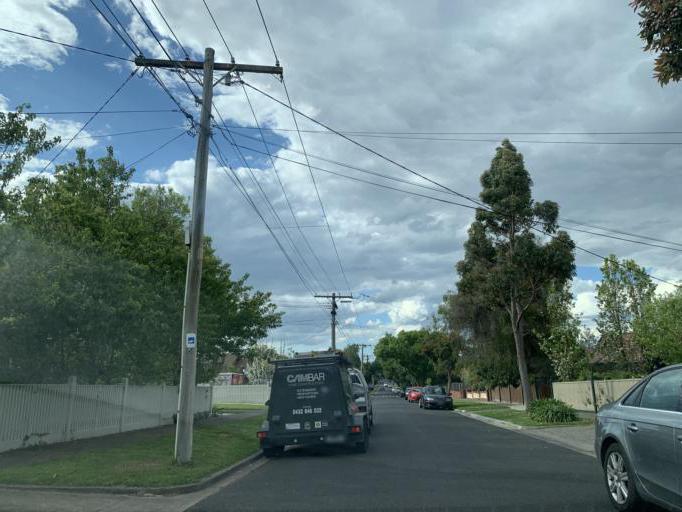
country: AU
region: Victoria
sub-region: Bayside
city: Hampton
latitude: -37.9312
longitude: 145.0013
